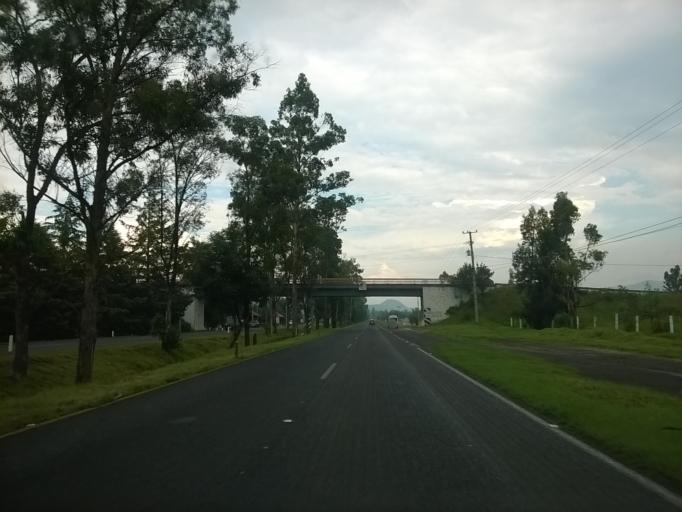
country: MX
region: Michoacan
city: Cuanajo
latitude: 19.5373
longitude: -101.5242
